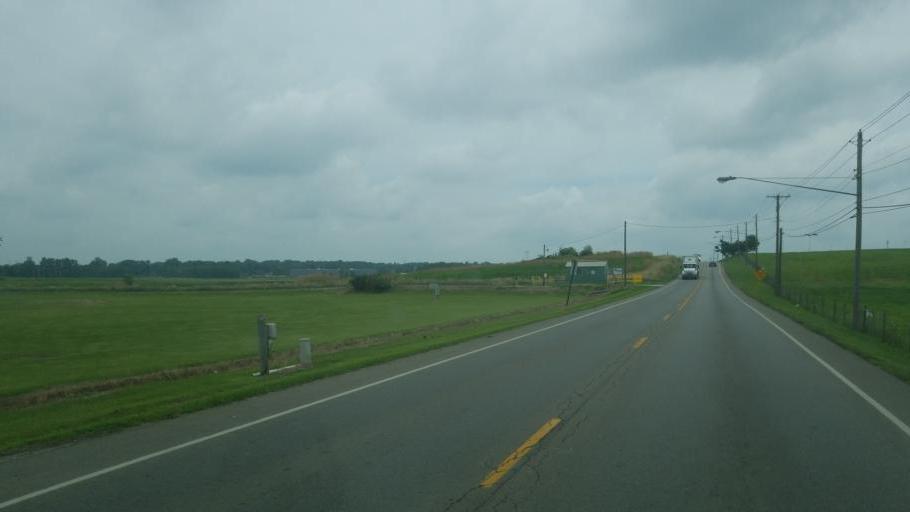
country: US
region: Ohio
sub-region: Richland County
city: Mansfield
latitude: 40.7835
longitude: -82.5135
